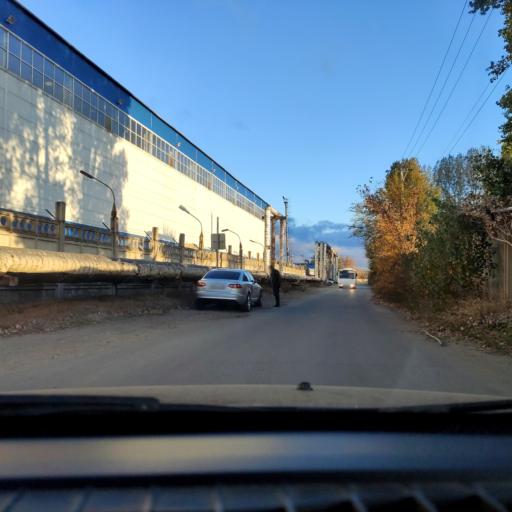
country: RU
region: Samara
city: Tol'yatti
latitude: 53.5773
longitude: 49.2632
